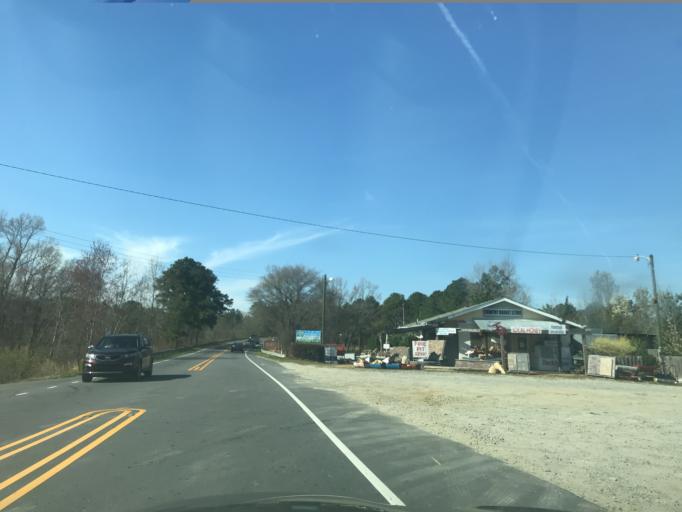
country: US
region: North Carolina
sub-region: Harnett County
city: Angier
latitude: 35.5506
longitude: -78.7557
